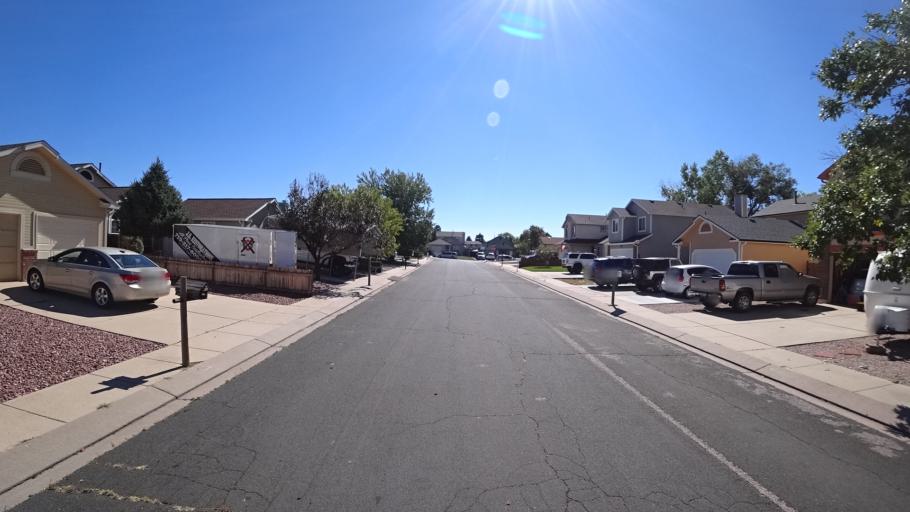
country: US
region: Colorado
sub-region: El Paso County
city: Stratmoor
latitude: 38.8119
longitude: -104.7406
